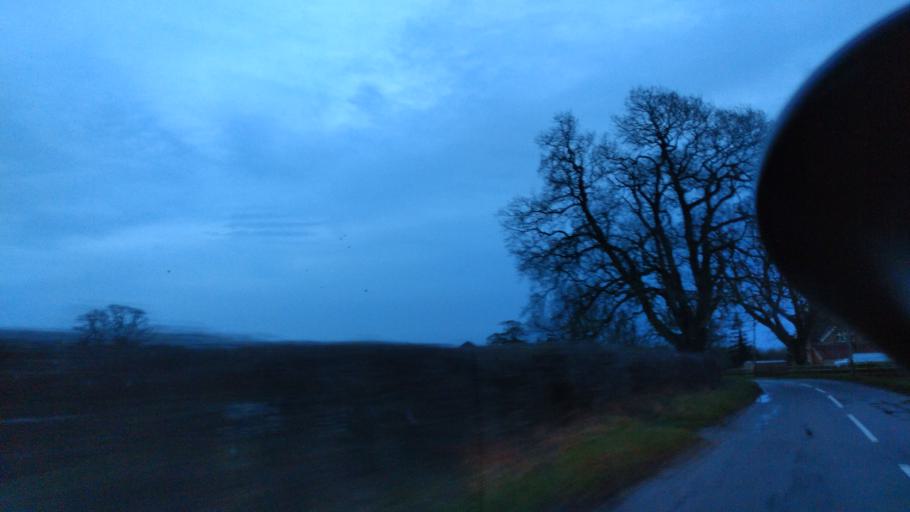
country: GB
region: England
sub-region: Oxfordshire
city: Shrivenham
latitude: 51.6052
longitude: -1.6672
